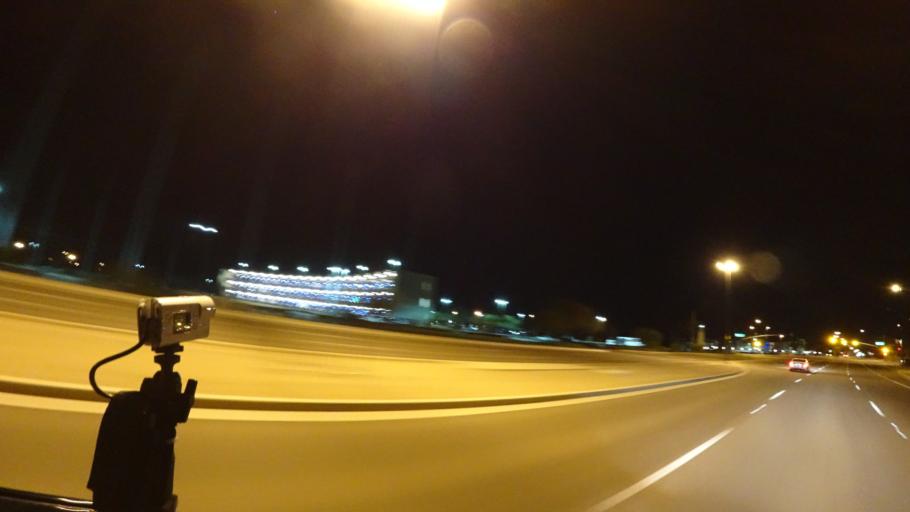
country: US
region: Arizona
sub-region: Maricopa County
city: Gilbert
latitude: 33.3214
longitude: -111.7412
